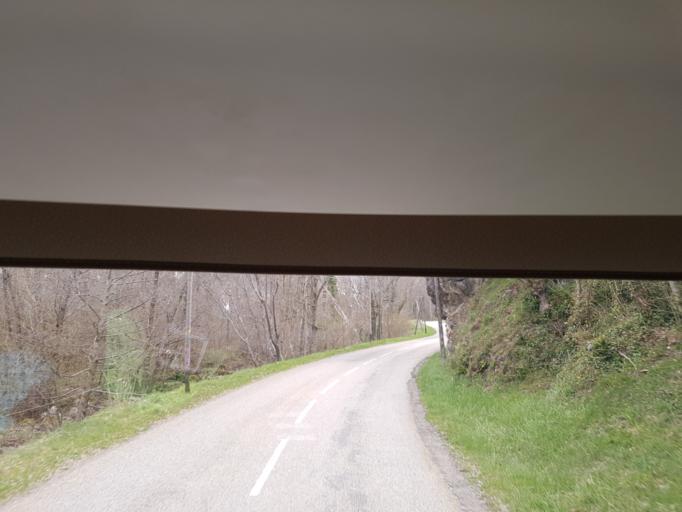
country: FR
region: Languedoc-Roussillon
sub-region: Departement de l'Aude
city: Quillan
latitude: 42.7383
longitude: 2.0874
